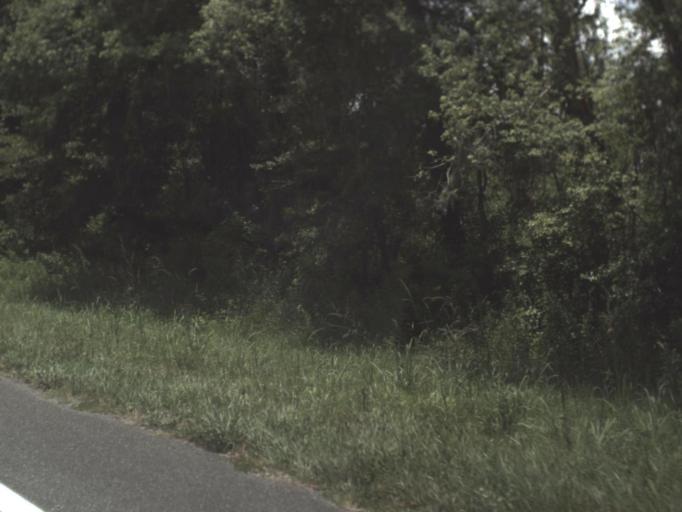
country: US
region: Florida
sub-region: Columbia County
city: Five Points
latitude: 30.2175
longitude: -82.6552
